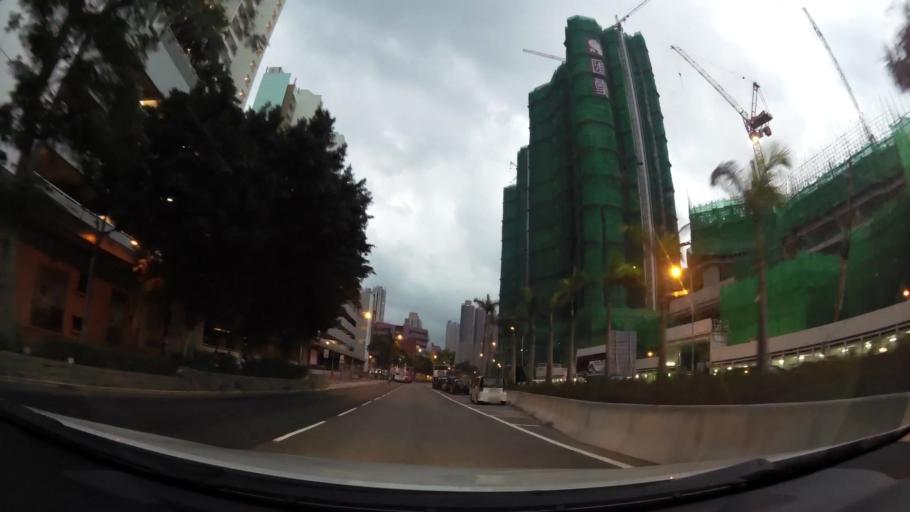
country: HK
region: Sham Shui Po
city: Sham Shui Po
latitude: 22.3288
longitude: 114.1530
